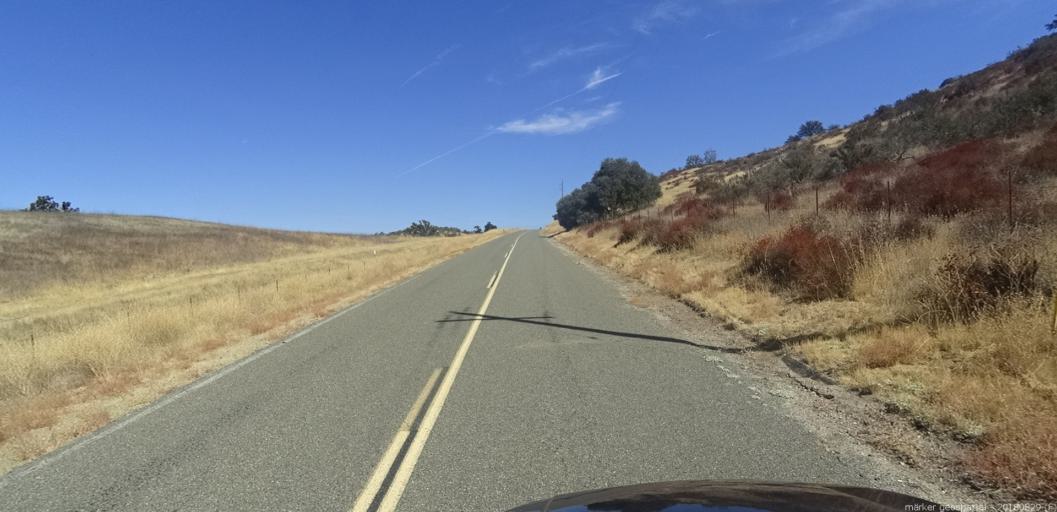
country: US
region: California
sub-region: San Luis Obispo County
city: Lake Nacimiento
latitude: 35.8223
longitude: -120.9803
